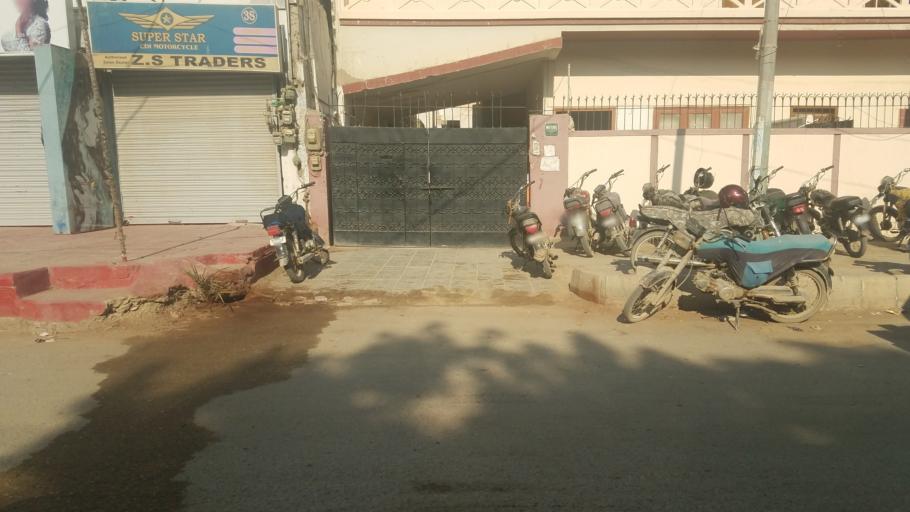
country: PK
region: Sindh
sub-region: Karachi District
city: Karachi
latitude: 24.9356
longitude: 67.0638
